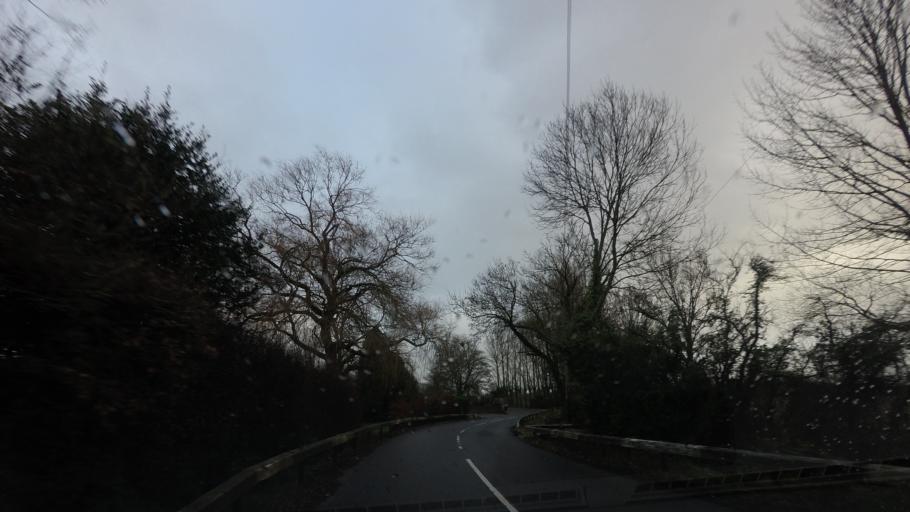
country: GB
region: England
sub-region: Kent
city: Marden
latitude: 51.1838
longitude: 0.4827
